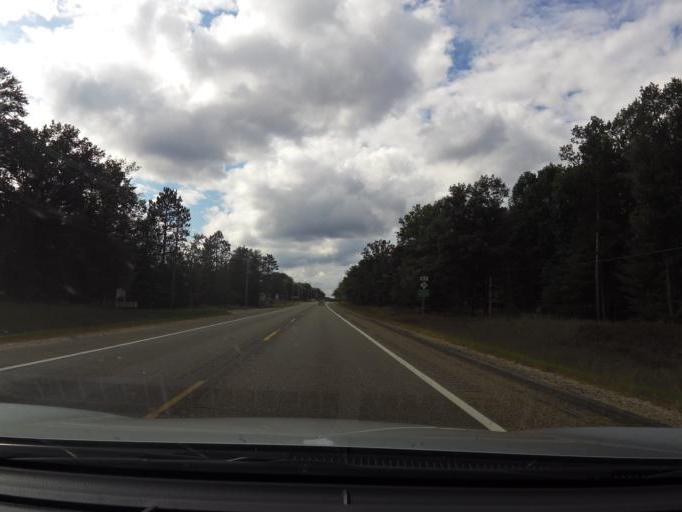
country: US
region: Michigan
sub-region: Roscommon County
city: Prudenville
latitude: 44.3054
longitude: -84.6119
